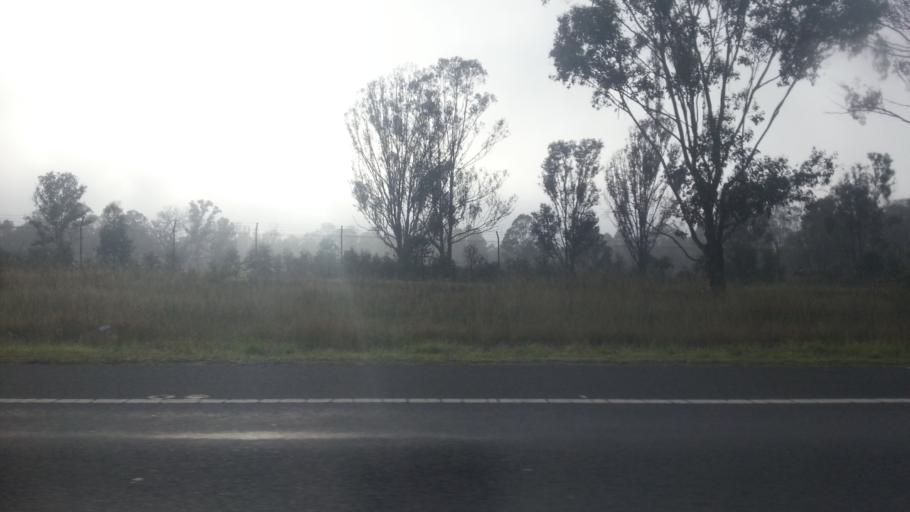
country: AU
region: New South Wales
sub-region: Penrith Municipality
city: Glenmore Park
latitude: -33.8238
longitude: 150.6843
